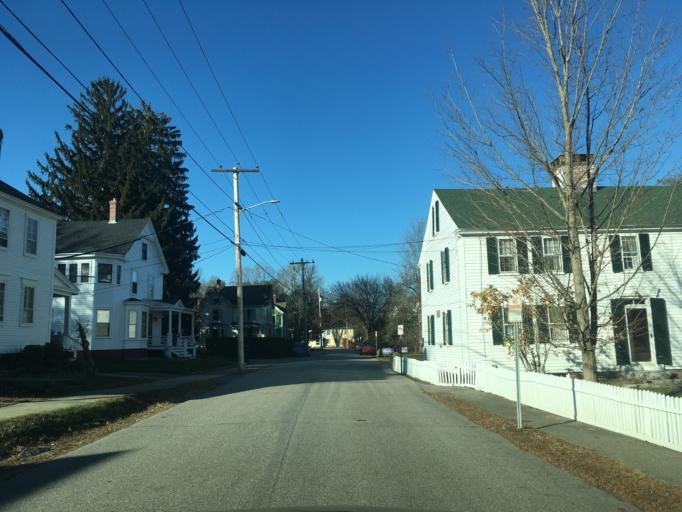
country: US
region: New Hampshire
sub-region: Rockingham County
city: Exeter
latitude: 42.9832
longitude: -70.9546
